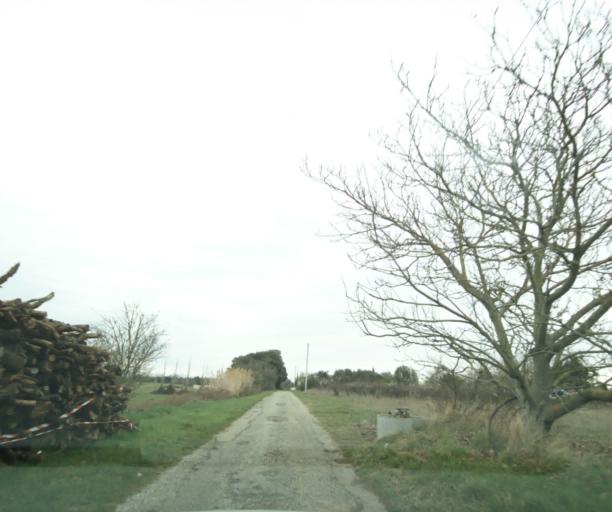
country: FR
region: Rhone-Alpes
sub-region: Departement de la Drome
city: Bourg-les-Valence
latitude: 44.9695
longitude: 4.8906
